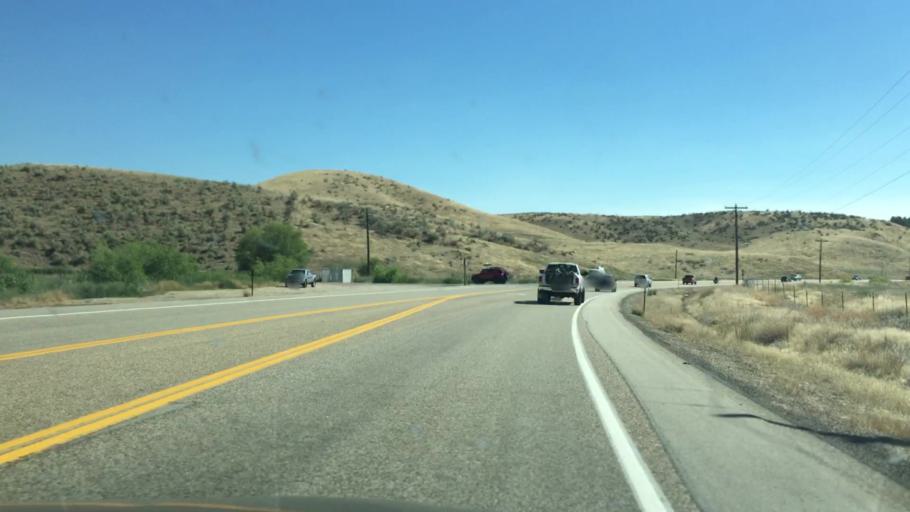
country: US
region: Idaho
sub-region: Ada County
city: Eagle
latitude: 43.7307
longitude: -116.3045
